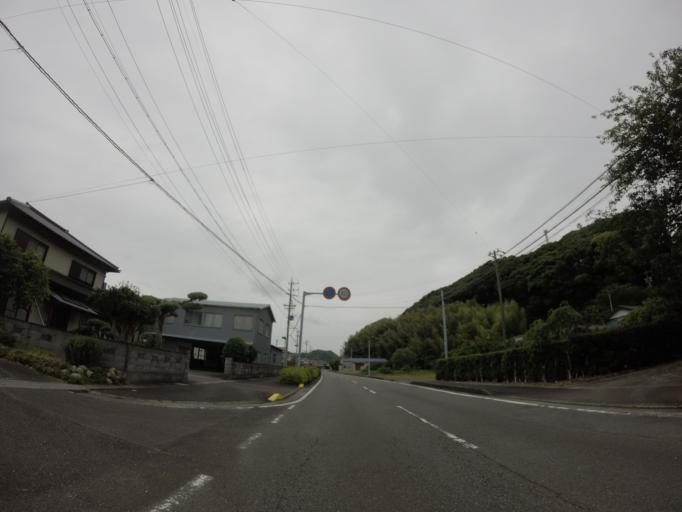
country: JP
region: Shizuoka
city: Shimada
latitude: 34.8019
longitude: 138.1951
